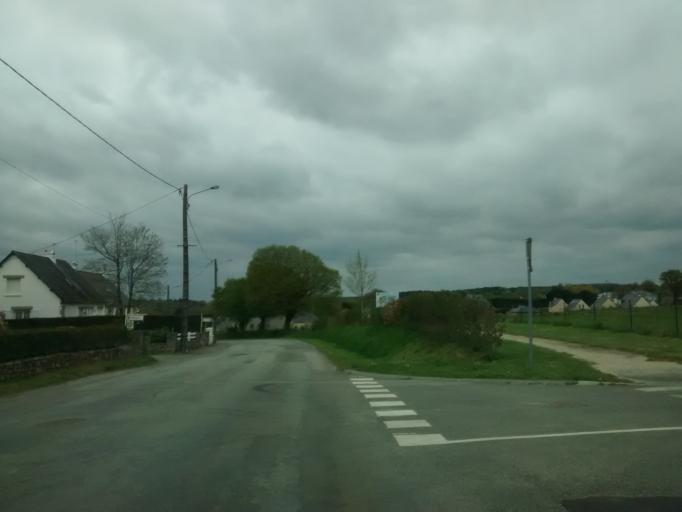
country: FR
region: Brittany
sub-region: Departement du Morbihan
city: Malestroit
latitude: 47.8040
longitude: -2.4126
